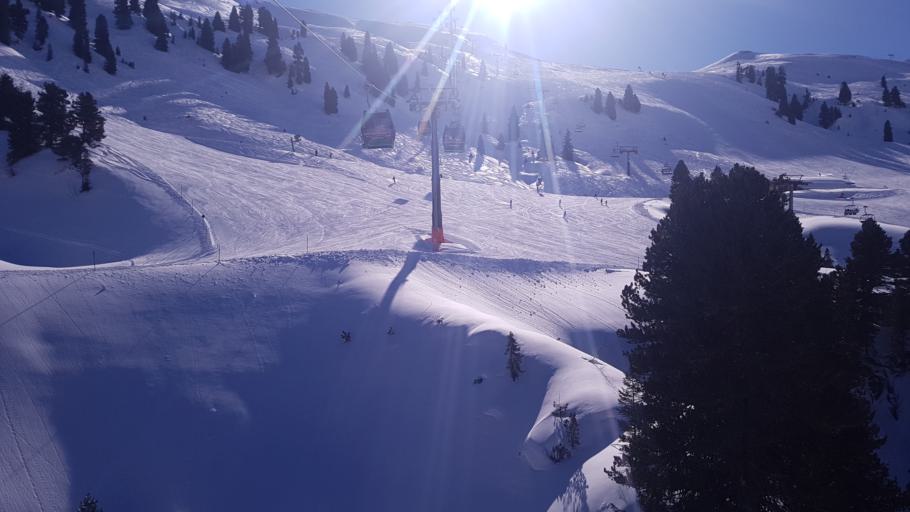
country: AT
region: Salzburg
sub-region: Politischer Bezirk Zell am See
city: Neukirchen am Grossvenediger
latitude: 47.2921
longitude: 12.2864
